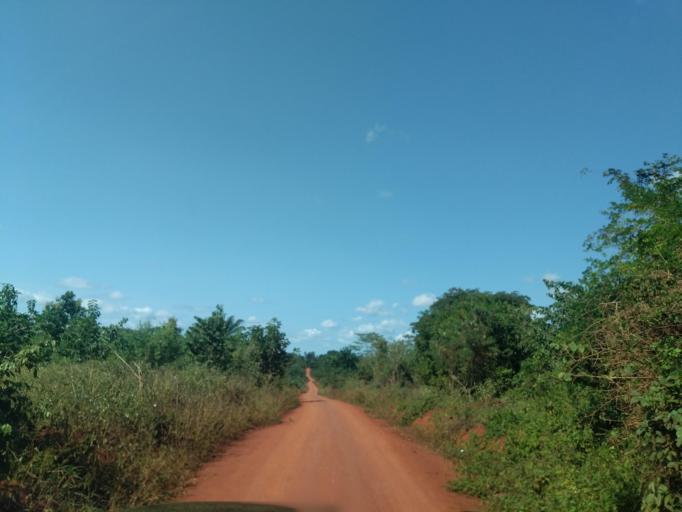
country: TZ
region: Tanga
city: Muheza
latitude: -5.3756
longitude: 38.5809
